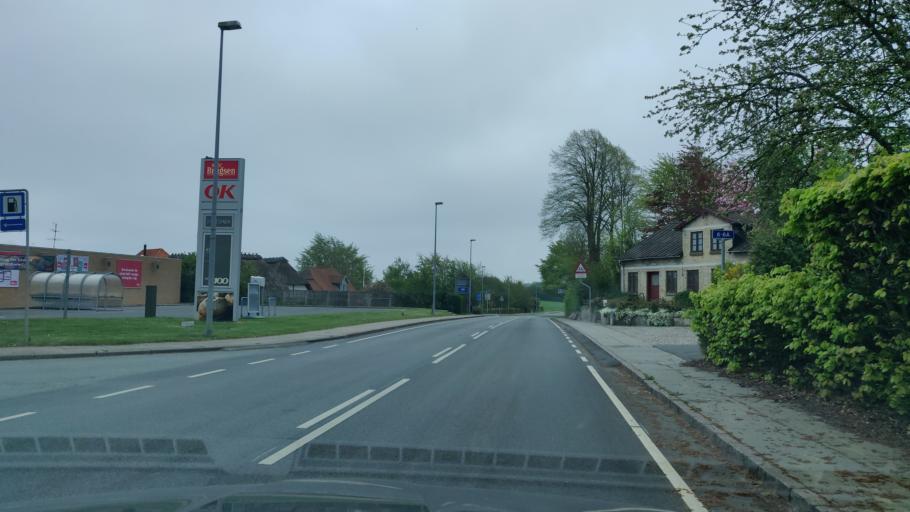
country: DK
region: South Denmark
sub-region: Sonderborg Kommune
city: Guderup
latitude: 54.9864
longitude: 9.9783
